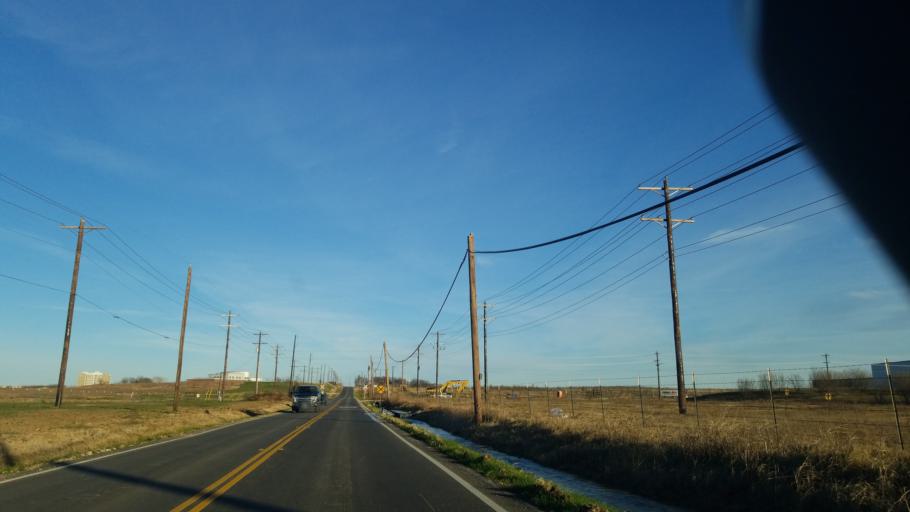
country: US
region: Texas
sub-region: Denton County
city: Denton
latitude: 33.2193
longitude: -97.1842
